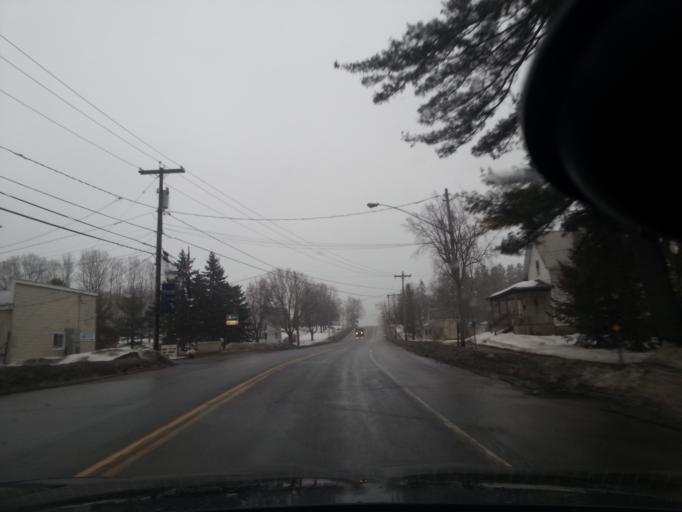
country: US
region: New York
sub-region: St. Lawrence County
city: Ogdensburg
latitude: 44.6156
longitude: -75.4034
